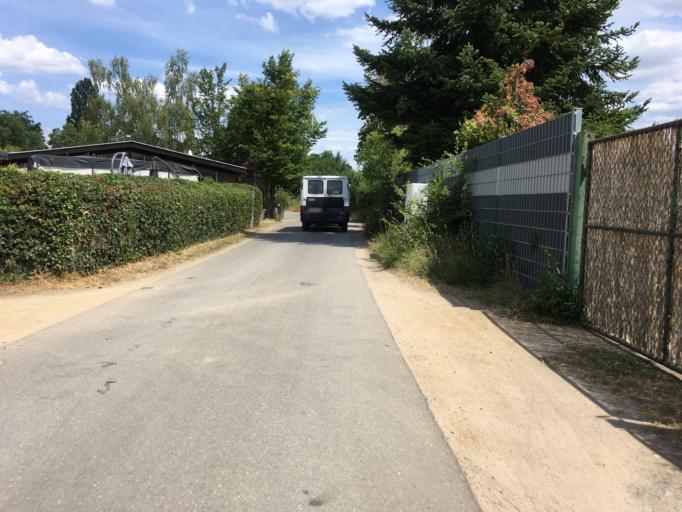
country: DE
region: Rheinland-Pfalz
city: Neuhofen
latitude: 49.4263
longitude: 8.4581
